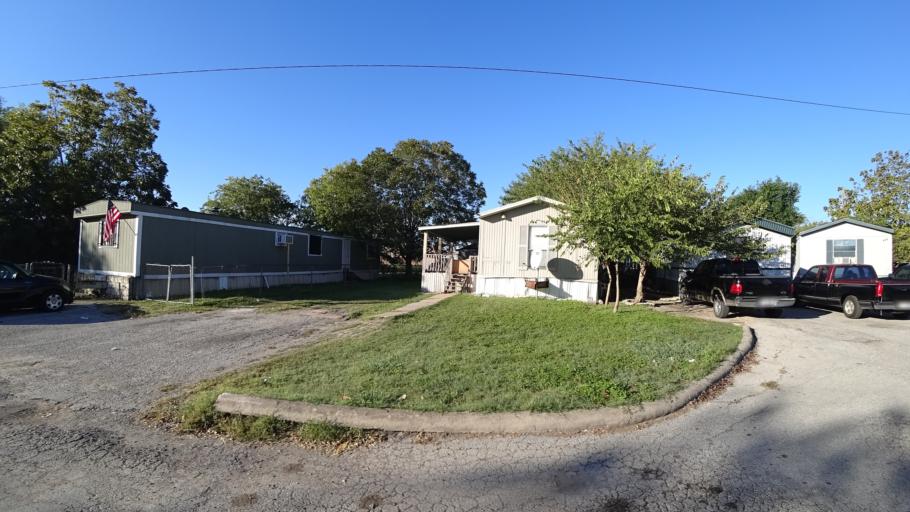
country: US
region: Texas
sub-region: Travis County
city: Austin
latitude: 30.2272
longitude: -97.6945
